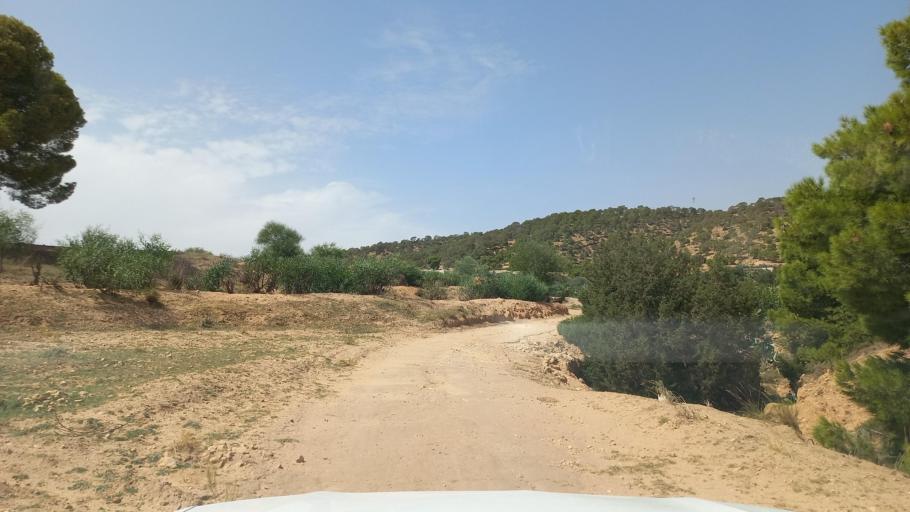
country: TN
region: Al Qasrayn
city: Kasserine
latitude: 35.3782
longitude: 8.9131
